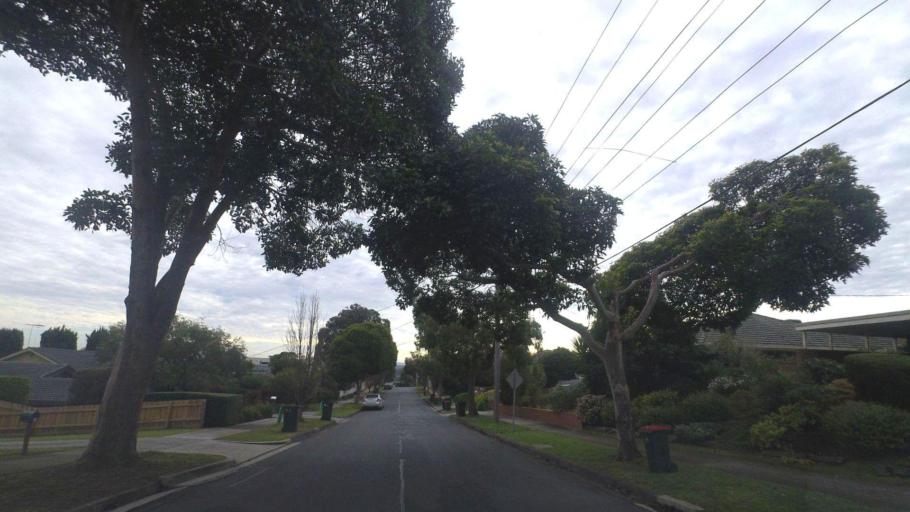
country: AU
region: Victoria
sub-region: Manningham
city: Templestowe Lower
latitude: -37.7634
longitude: 145.1051
